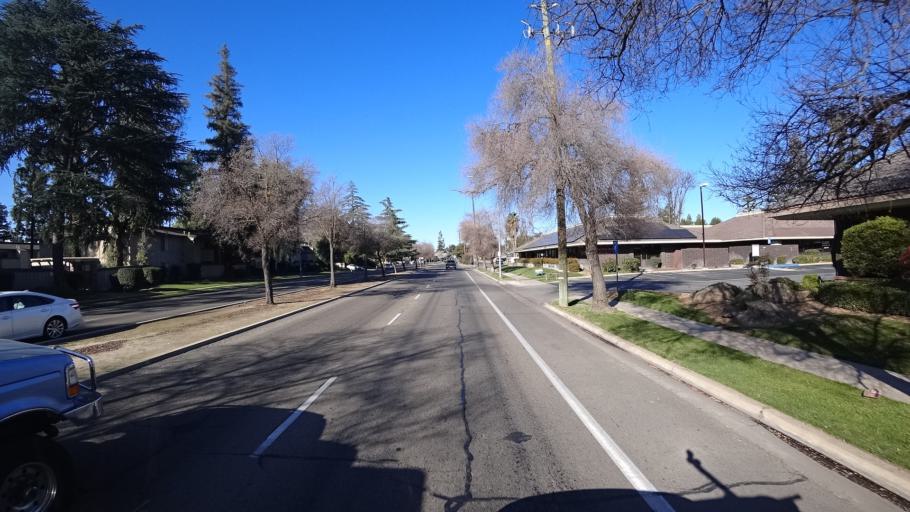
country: US
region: California
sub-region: Fresno County
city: Clovis
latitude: 36.8232
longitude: -119.7557
